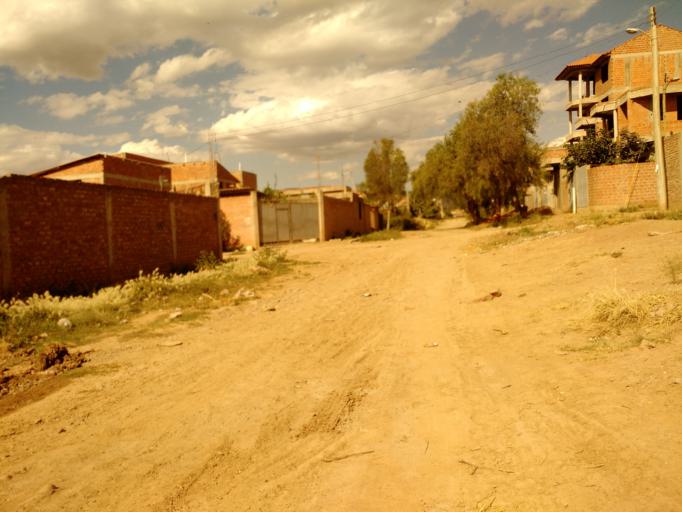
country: BO
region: Cochabamba
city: Cochabamba
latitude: -17.4592
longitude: -66.1503
